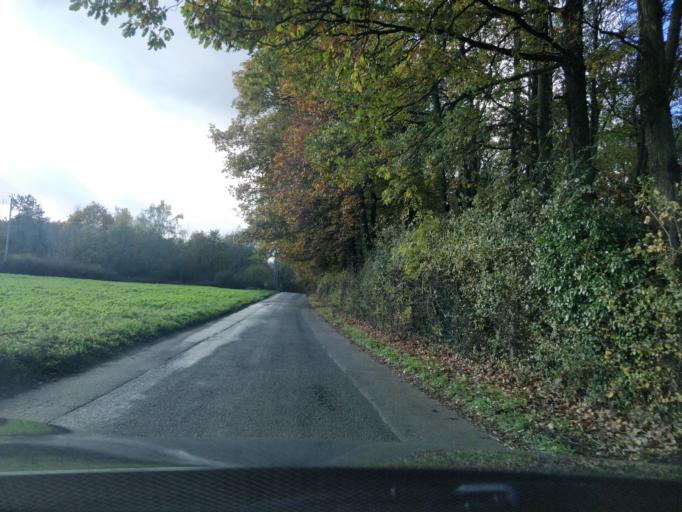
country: FR
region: Ile-de-France
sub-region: Departement de l'Essonne
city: Briis-sous-Forges
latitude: 48.6295
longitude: 2.1364
